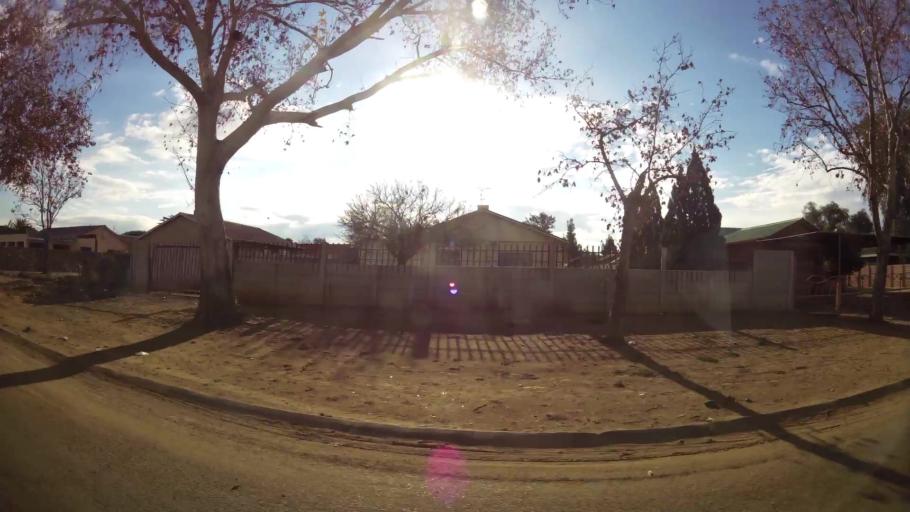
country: ZA
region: Orange Free State
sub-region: Lejweleputswa District Municipality
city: Welkom
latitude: -27.9909
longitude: 26.7509
